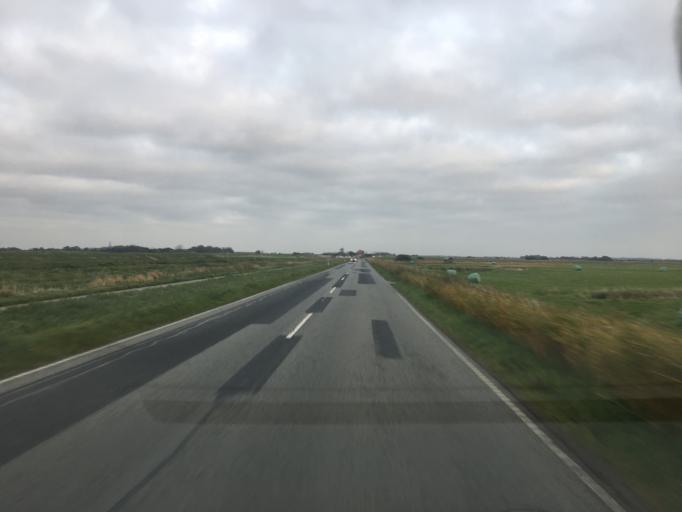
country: DE
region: Schleswig-Holstein
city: Rodenas
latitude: 54.9628
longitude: 8.7200
